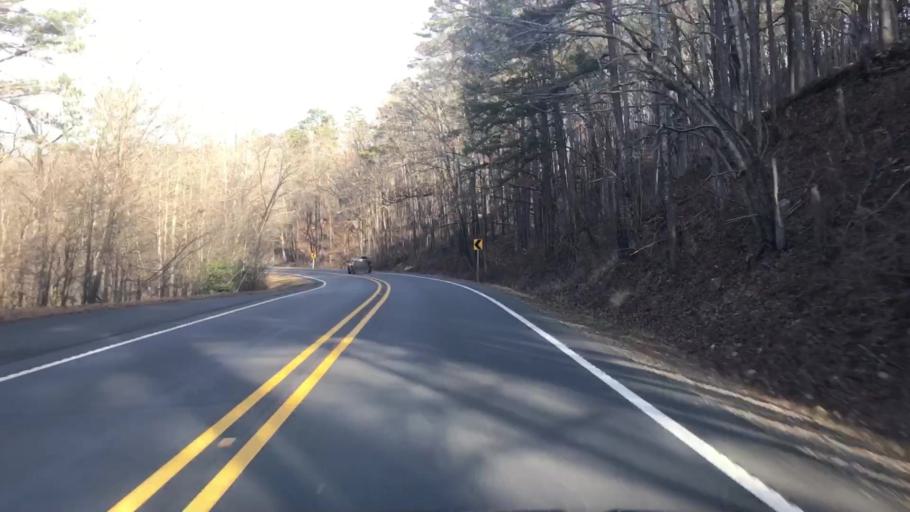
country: US
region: Arkansas
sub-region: Montgomery County
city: Mount Ida
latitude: 34.5219
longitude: -93.3907
